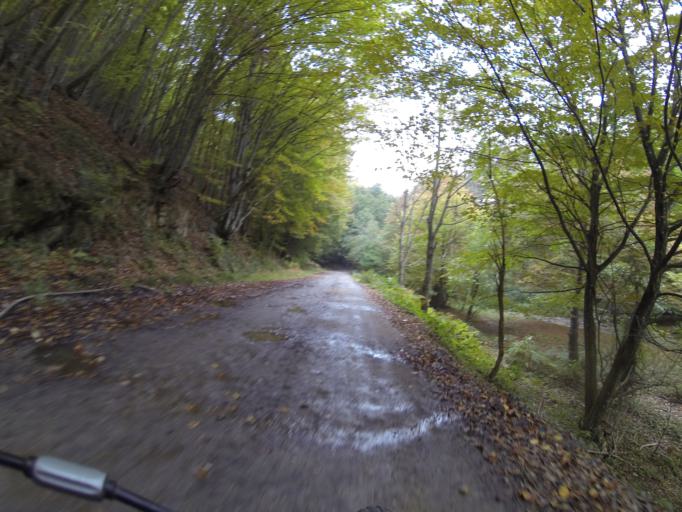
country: RO
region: Gorj
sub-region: Comuna Tismana
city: Sohodol
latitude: 45.0661
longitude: 22.8928
